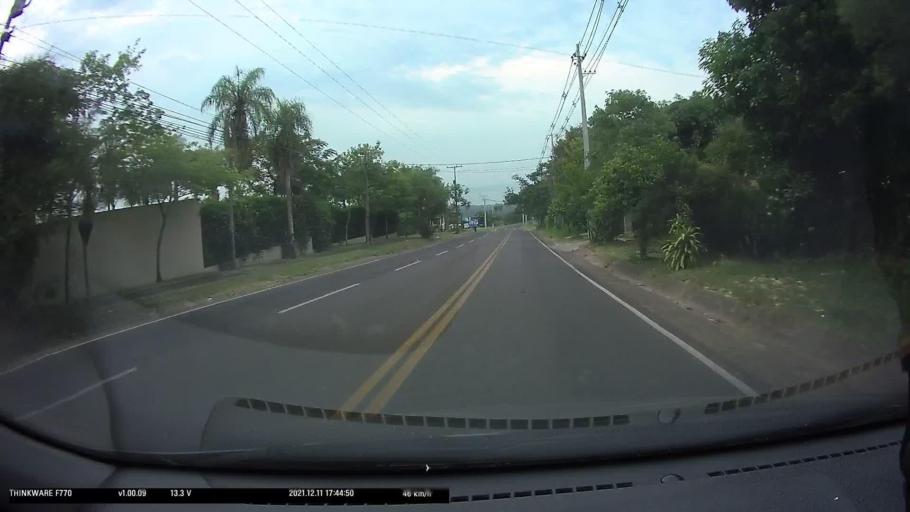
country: PY
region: Cordillera
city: San Bernardino
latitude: -25.2988
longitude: -57.2724
